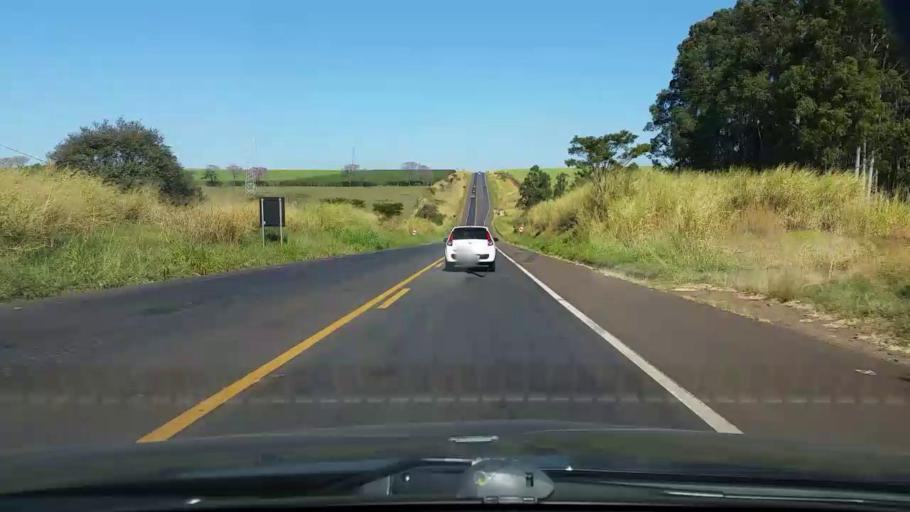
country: BR
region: Sao Paulo
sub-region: Jau
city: Jau
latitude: -22.3465
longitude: -48.5724
